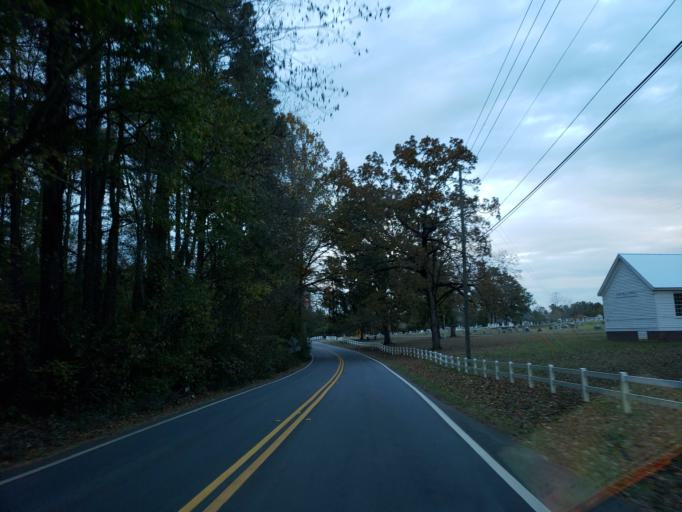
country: US
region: Georgia
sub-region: Cobb County
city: Acworth
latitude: 34.0235
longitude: -84.6835
